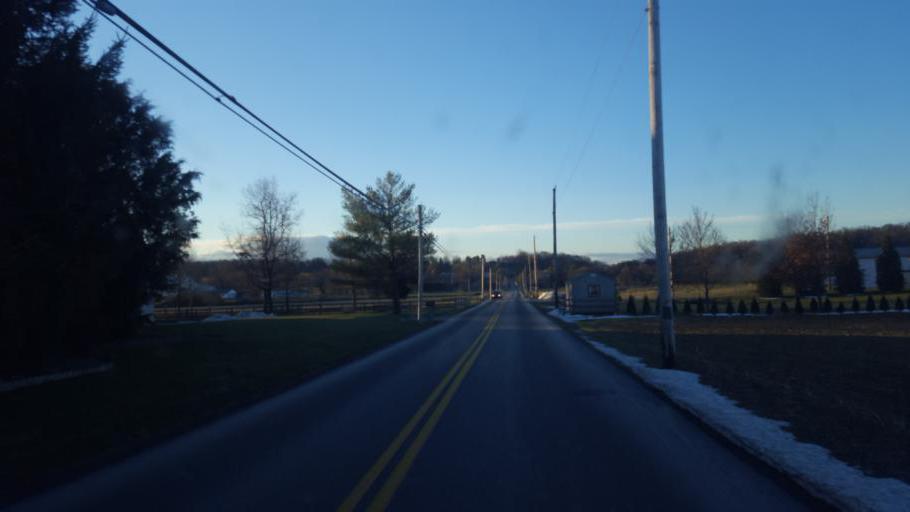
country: US
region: Pennsylvania
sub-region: Lancaster County
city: New Holland
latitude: 40.0856
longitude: -76.0877
